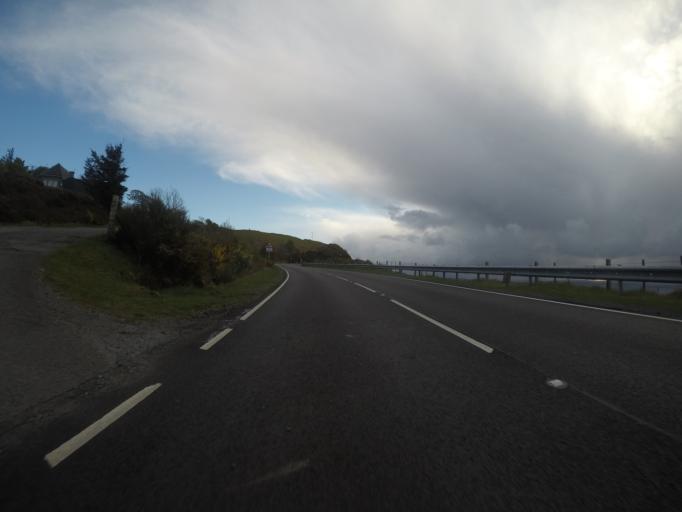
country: GB
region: Scotland
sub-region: Highland
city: Portree
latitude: 57.5820
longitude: -6.3595
